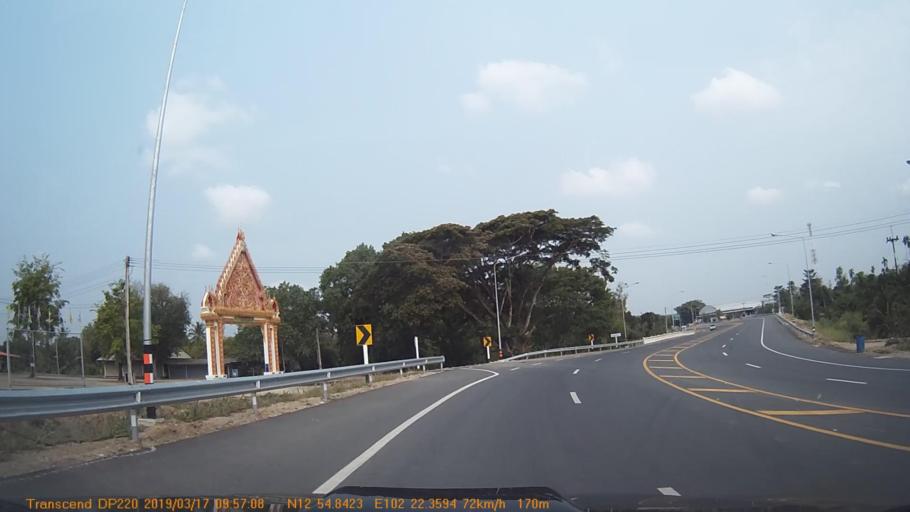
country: TH
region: Chanthaburi
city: Pong Nam Ron
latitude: 12.9157
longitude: 102.3709
